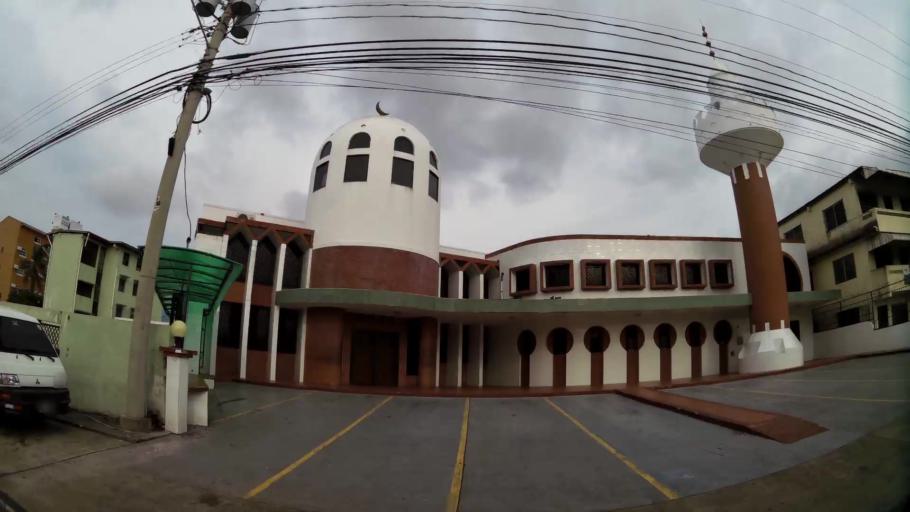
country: PA
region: Panama
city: Panama
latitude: 9.0010
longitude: -79.5216
